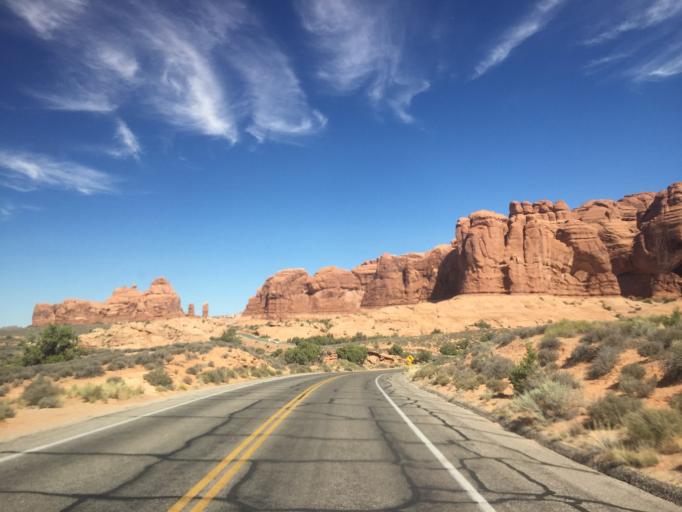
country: US
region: Utah
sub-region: Grand County
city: Moab
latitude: 38.6886
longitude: -109.5429
